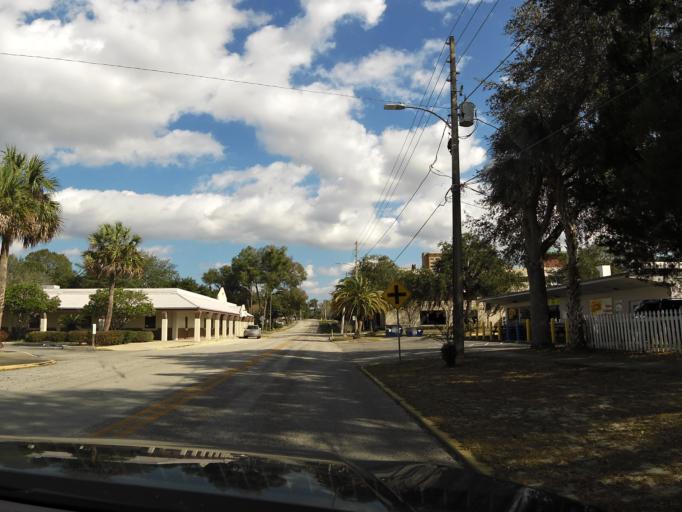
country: US
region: Florida
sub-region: Volusia County
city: DeLand
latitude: 29.0299
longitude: -81.3024
